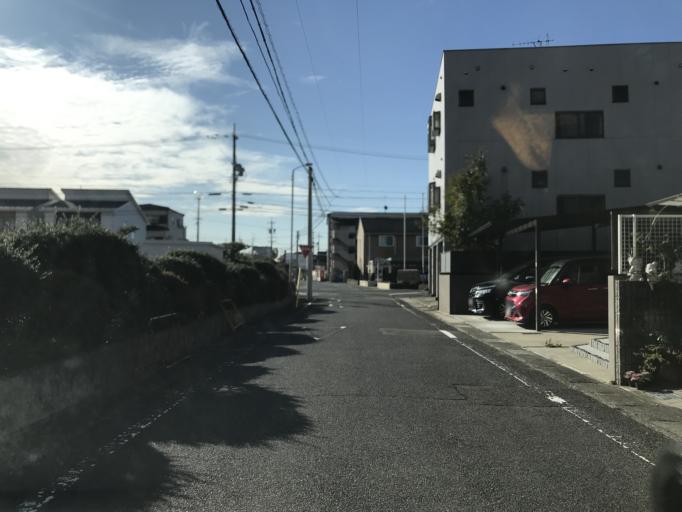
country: JP
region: Aichi
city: Inazawa
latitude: 35.2167
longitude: 136.8363
